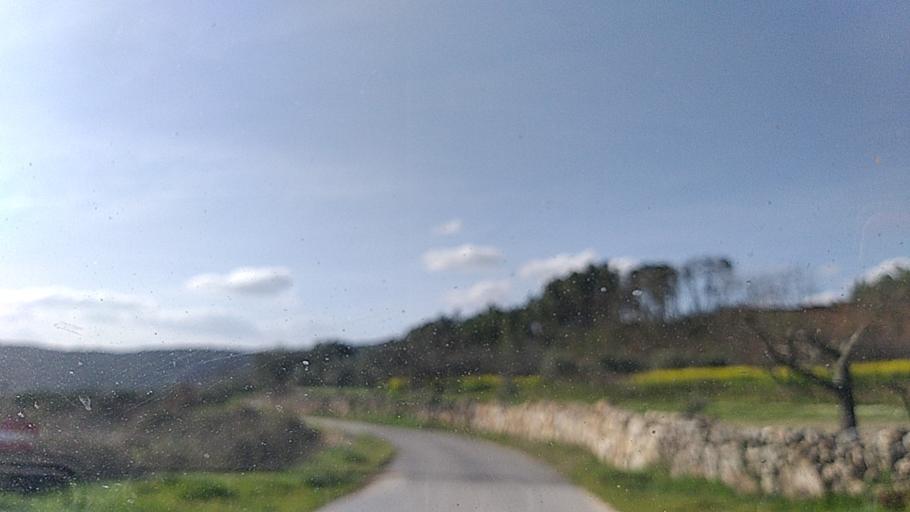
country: PT
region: Guarda
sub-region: Celorico da Beira
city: Celorico da Beira
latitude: 40.6550
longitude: -7.4068
